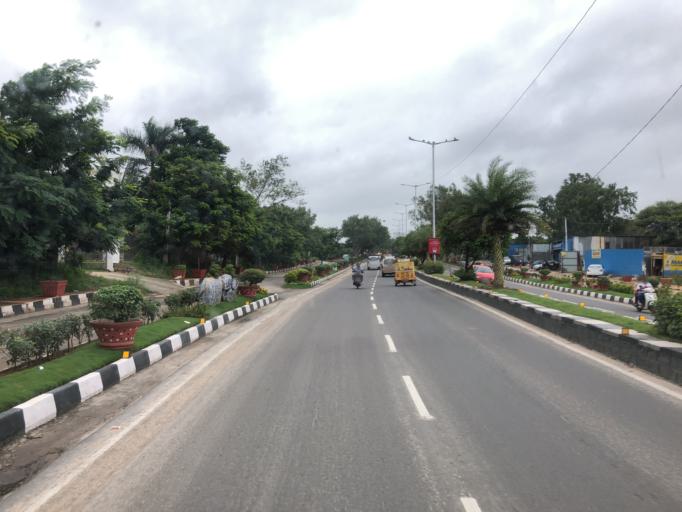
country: IN
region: Telangana
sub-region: Rangareddi
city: Kukatpalli
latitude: 17.4598
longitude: 78.3769
